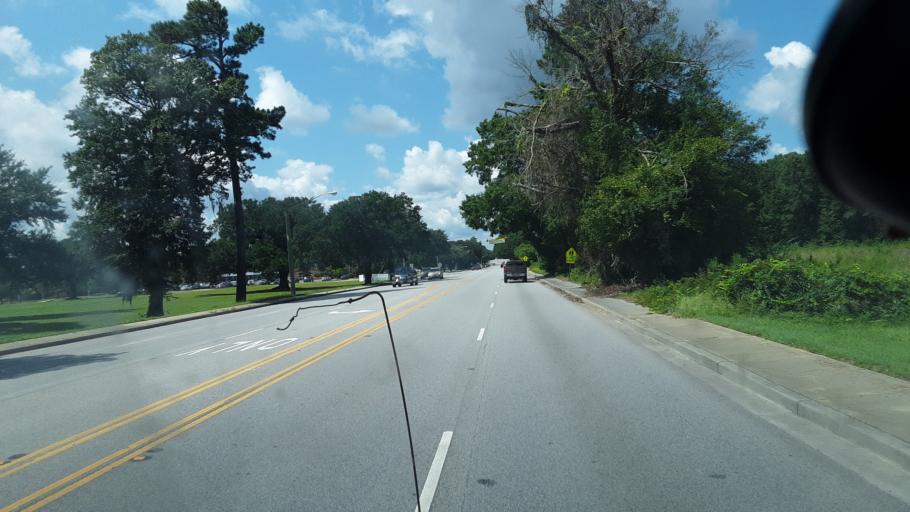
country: US
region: South Carolina
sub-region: Berkeley County
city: Moncks Corner
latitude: 33.2015
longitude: -79.9931
